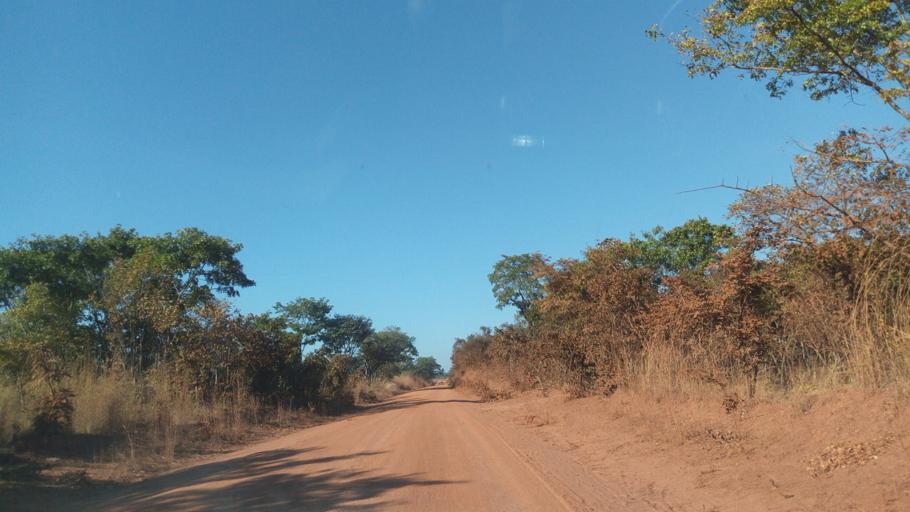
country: ZM
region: Luapula
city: Mwense
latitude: -10.6113
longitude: 28.4128
